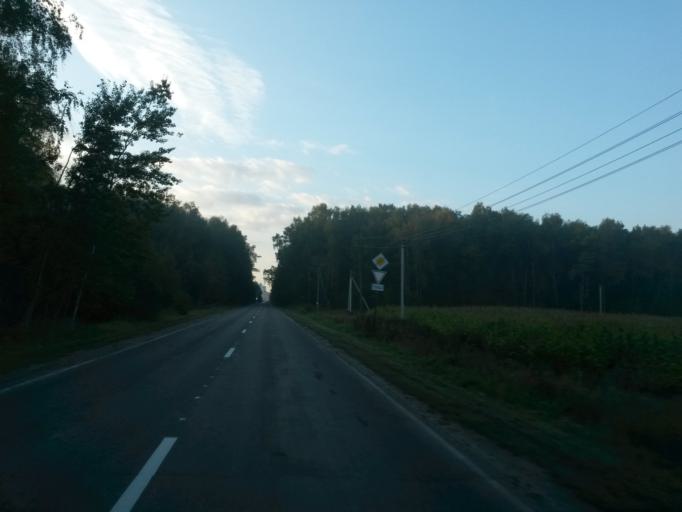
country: RU
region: Moskovskaya
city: Melikhovo
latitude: 55.1905
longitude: 37.7014
